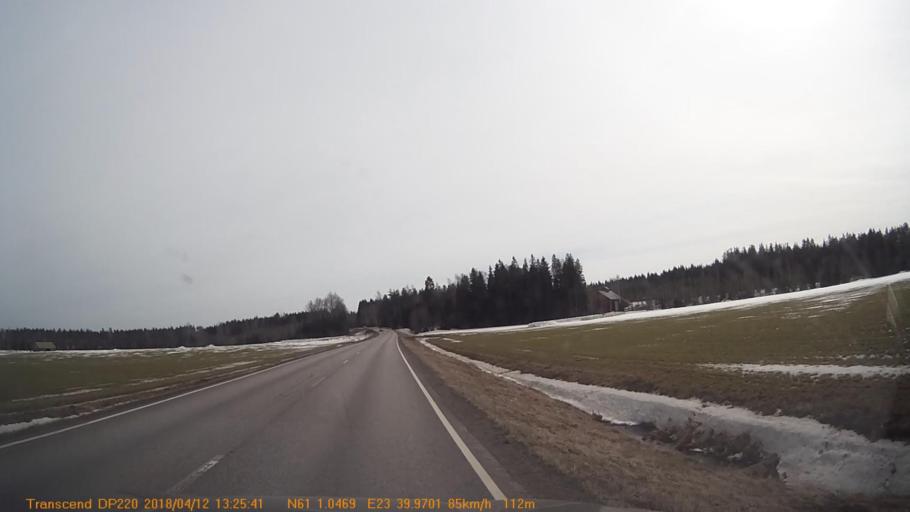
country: FI
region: Pirkanmaa
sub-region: Etelae-Pirkanmaa
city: Kylmaekoski
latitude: 61.0172
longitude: 23.6665
